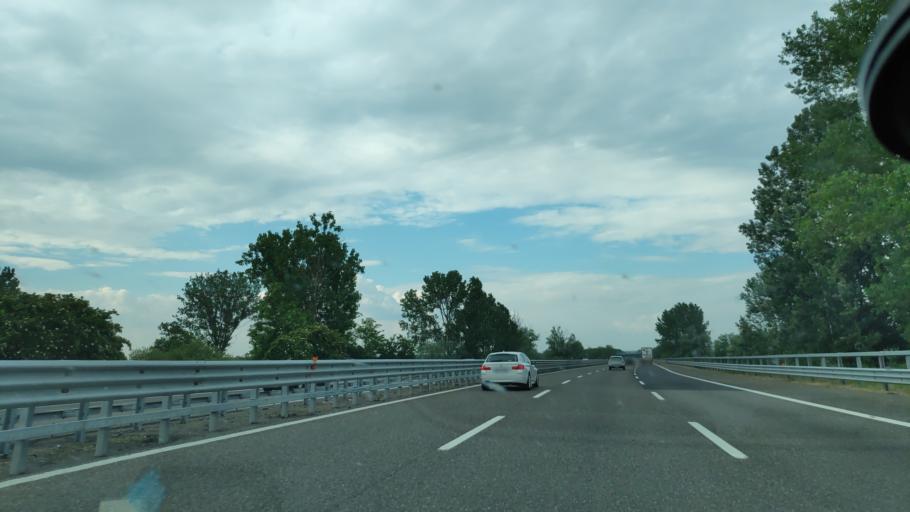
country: IT
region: Lombardy
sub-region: Provincia di Pavia
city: Pieve Albignola
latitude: 45.0972
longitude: 8.9691
